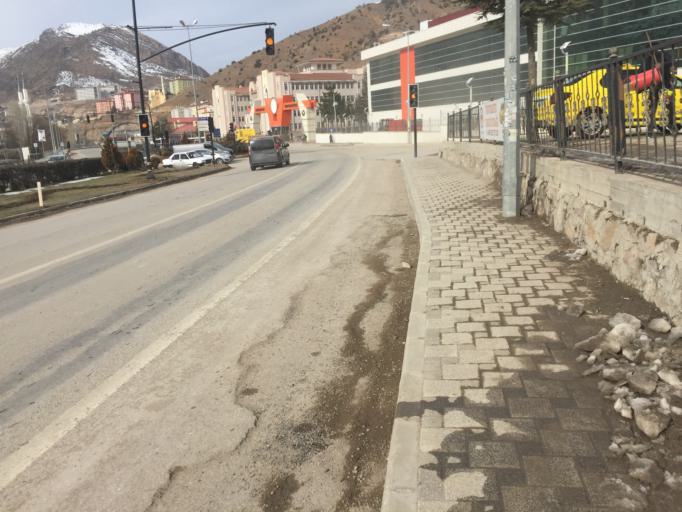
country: TR
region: Gumushane
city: Gumushkhane
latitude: 40.4348
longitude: 39.5176
